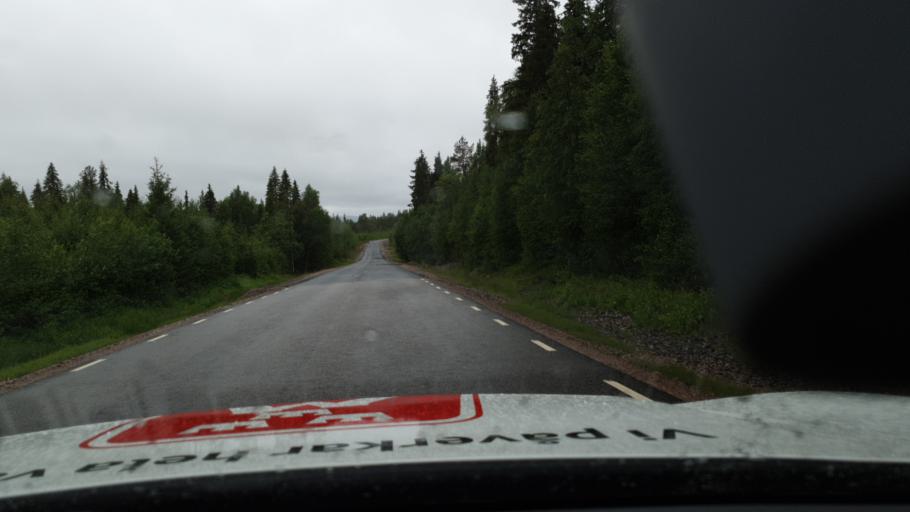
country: SE
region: Norrbotten
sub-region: Overtornea Kommun
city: OEvertornea
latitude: 66.5446
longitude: 23.3541
